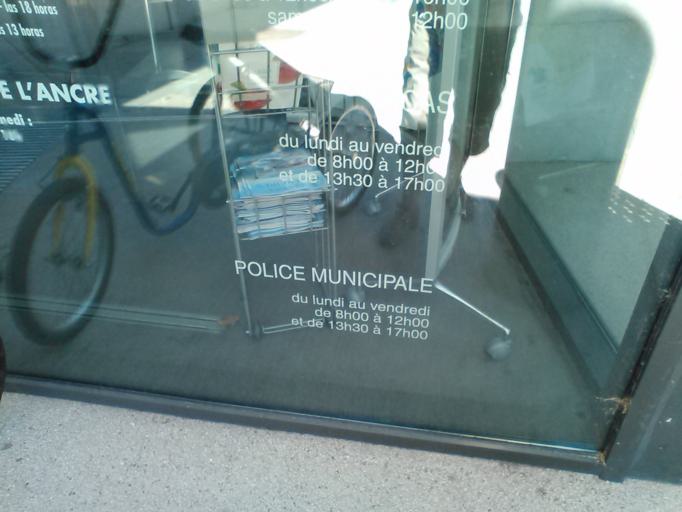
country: FR
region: Languedoc-Roussillon
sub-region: Departement de l'Herault
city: Perols
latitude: 43.5468
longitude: 3.9791
